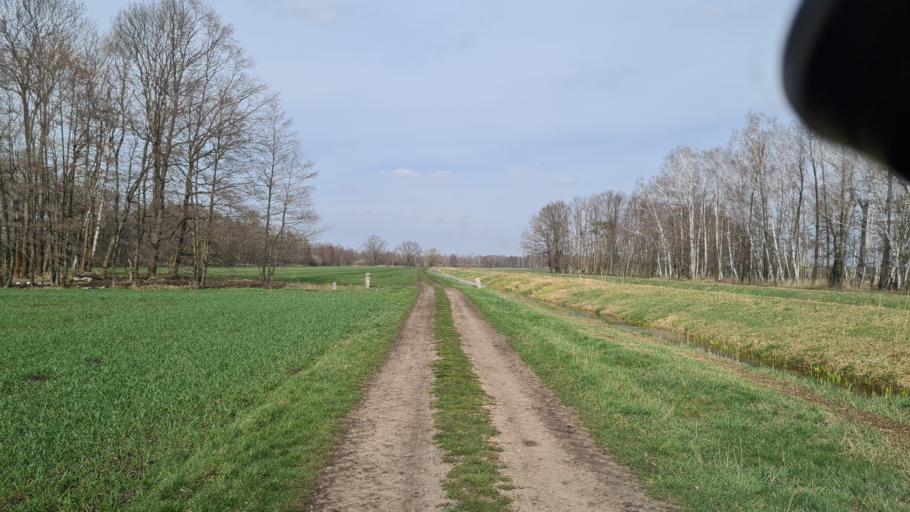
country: DE
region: Brandenburg
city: Bronkow
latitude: 51.6215
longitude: 13.9168
